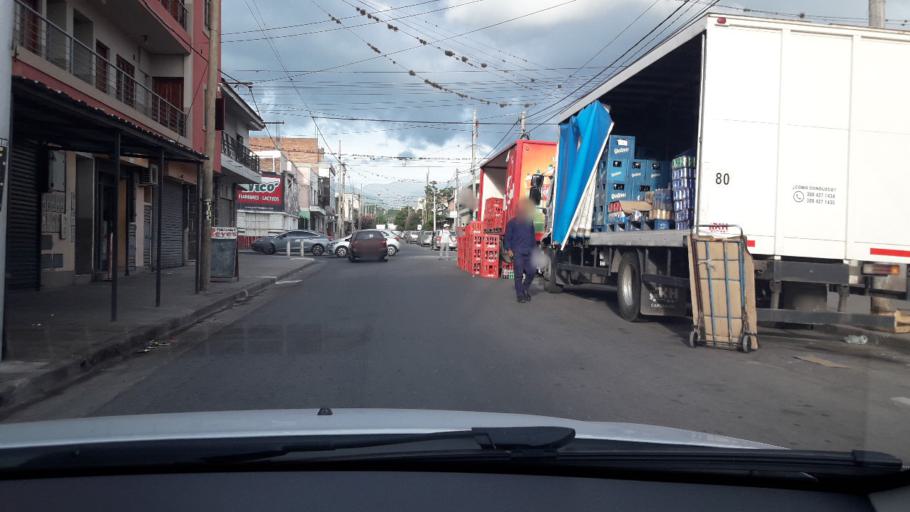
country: AR
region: Jujuy
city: San Salvador de Jujuy
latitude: -24.1916
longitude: -65.3045
